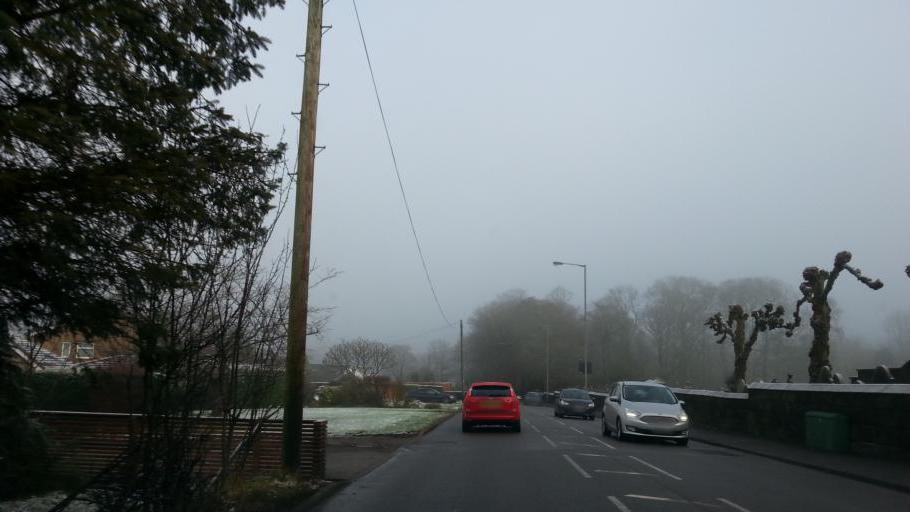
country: GB
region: England
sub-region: Staffordshire
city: Biddulph
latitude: 53.1283
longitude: -2.1663
